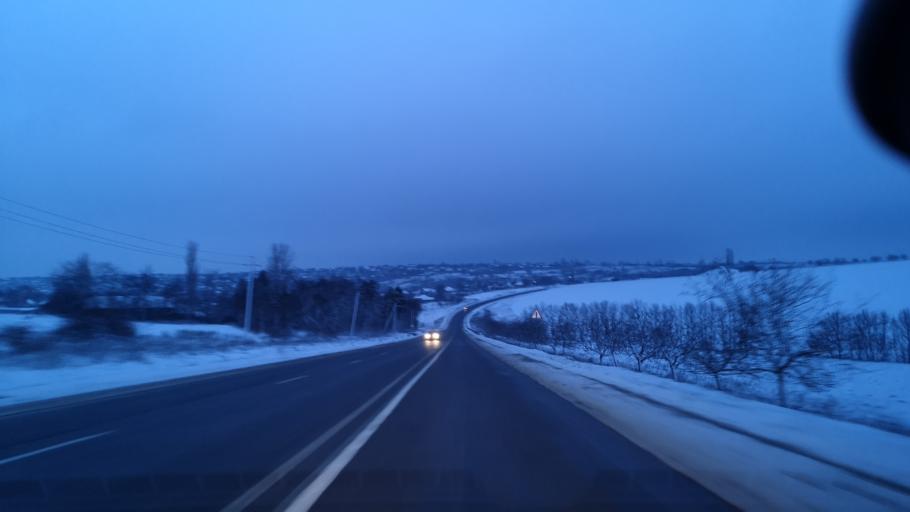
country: MD
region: Soldanesti
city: Soldanesti
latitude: 47.7090
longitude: 28.8472
